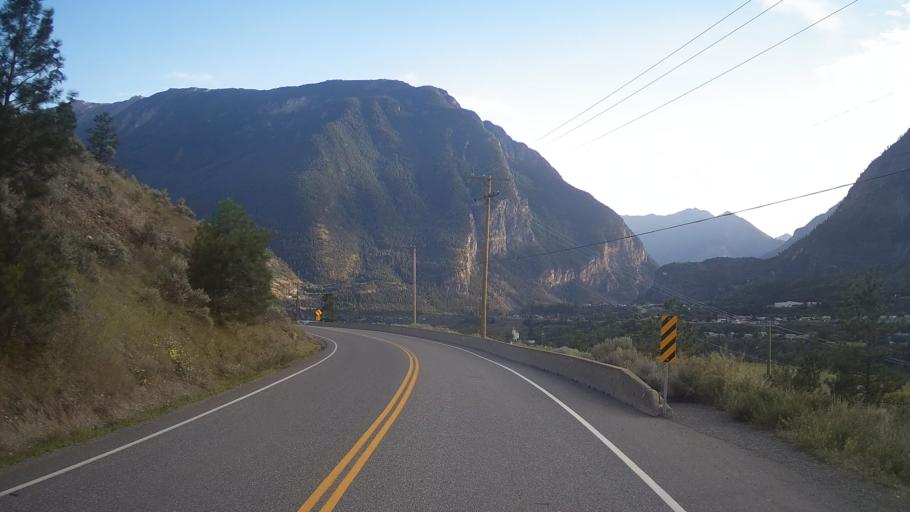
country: CA
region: British Columbia
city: Lillooet
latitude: 50.6943
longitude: -121.9202
